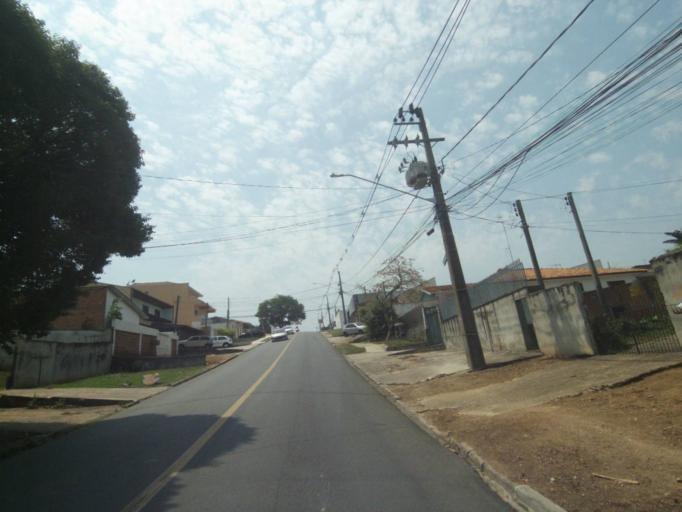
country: BR
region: Parana
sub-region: Sao Jose Dos Pinhais
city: Sao Jose dos Pinhais
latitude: -25.5346
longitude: -49.2465
